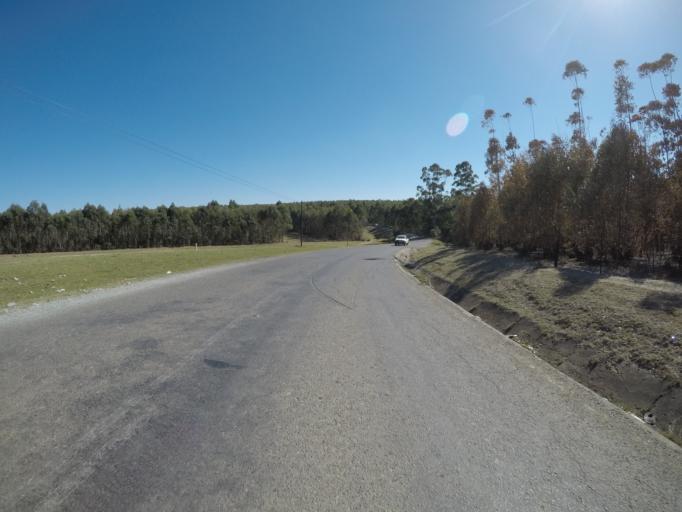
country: ZA
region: Eastern Cape
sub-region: OR Tambo District Municipality
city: Mthatha
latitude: -31.7775
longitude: 28.7372
